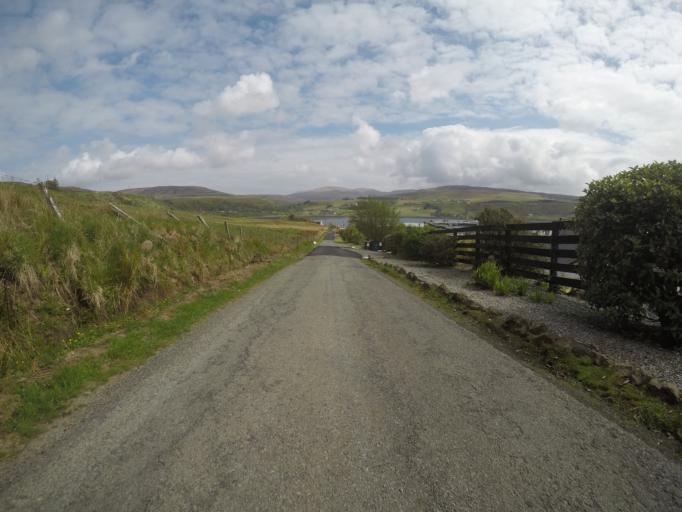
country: GB
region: Scotland
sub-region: Highland
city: Portree
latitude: 57.5880
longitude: -6.3818
